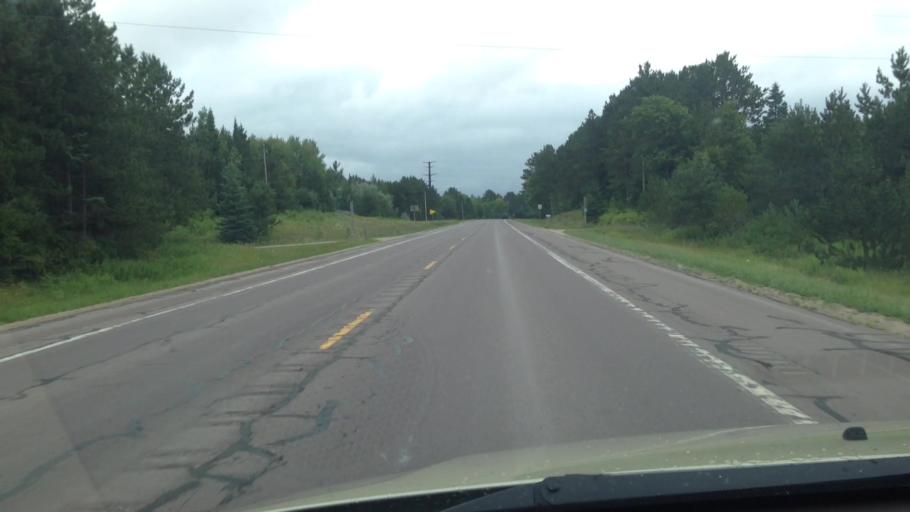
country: US
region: Michigan
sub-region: Schoolcraft County
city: Manistique
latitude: 46.0926
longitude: -85.9499
